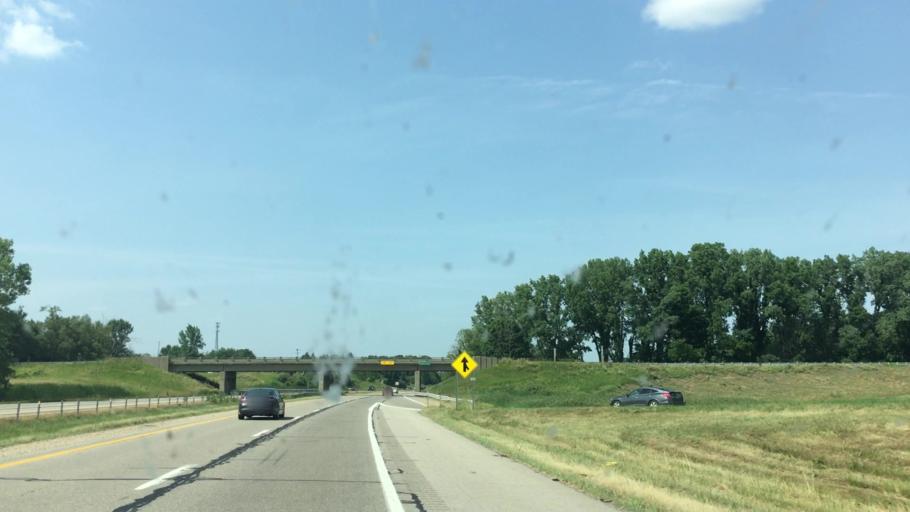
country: US
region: Michigan
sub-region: Allegan County
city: Wayland
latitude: 42.5928
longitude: -85.6627
